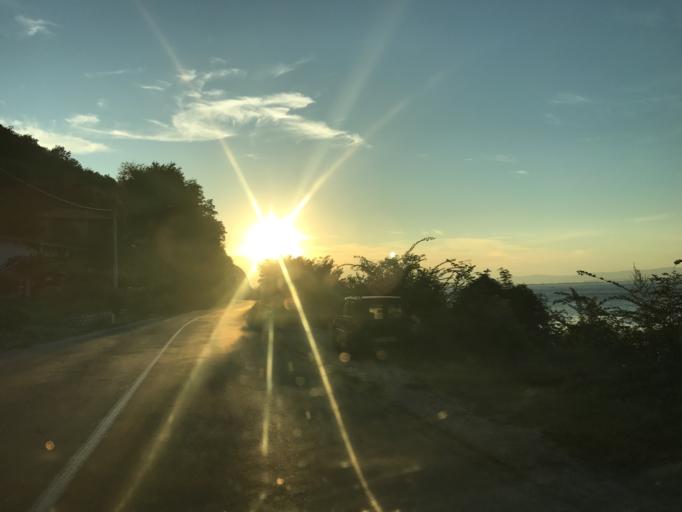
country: RO
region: Caras-Severin
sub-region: Comuna Pescari
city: Coronini
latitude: 44.6600
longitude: 21.6868
